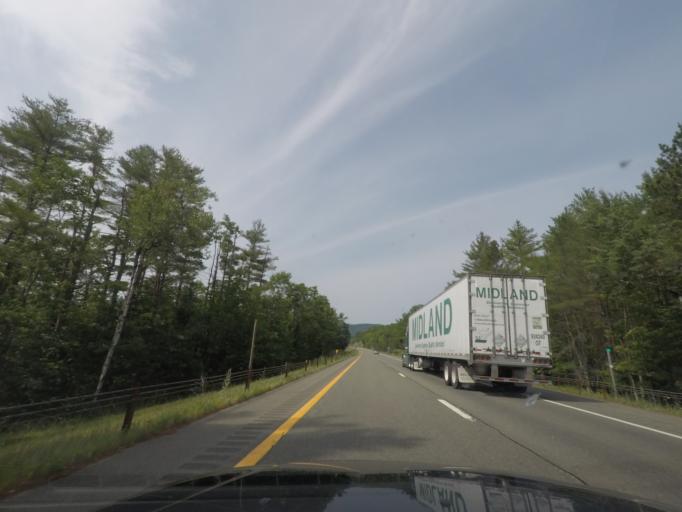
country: US
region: New York
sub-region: Essex County
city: Elizabethtown
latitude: 44.3584
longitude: -73.5312
